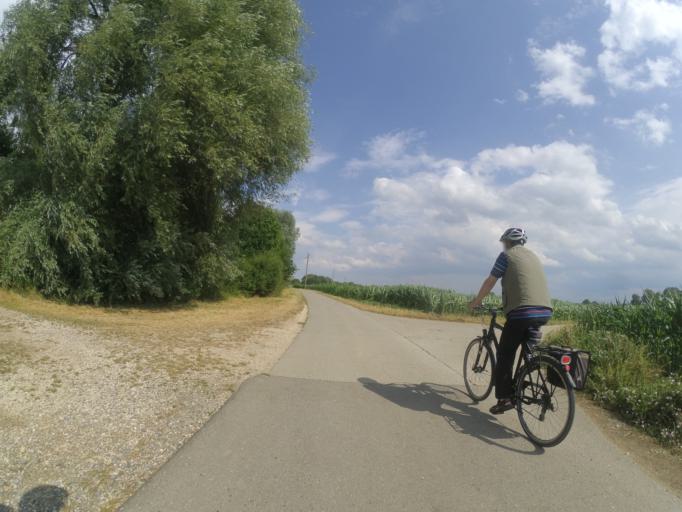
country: DE
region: Baden-Wuerttemberg
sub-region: Tuebingen Region
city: Opfingen
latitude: 48.2797
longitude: 9.8126
